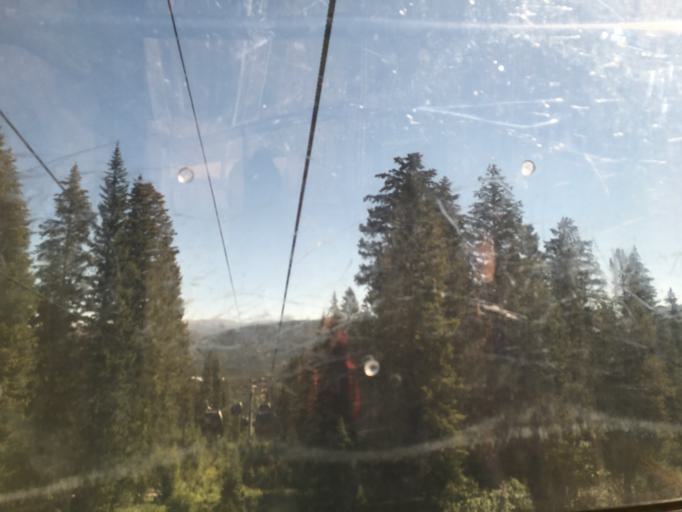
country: US
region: Colorado
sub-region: Summit County
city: Breckenridge
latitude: 39.4852
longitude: -106.0655
